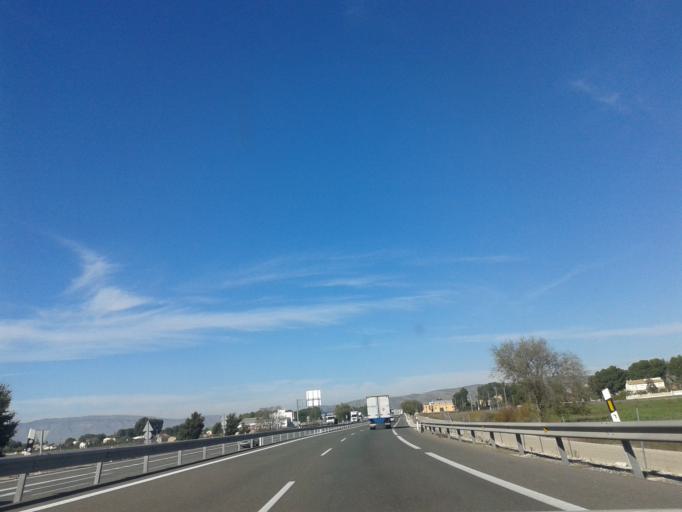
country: ES
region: Valencia
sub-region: Provincia de Alicante
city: Villena
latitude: 38.6507
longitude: -0.8724
